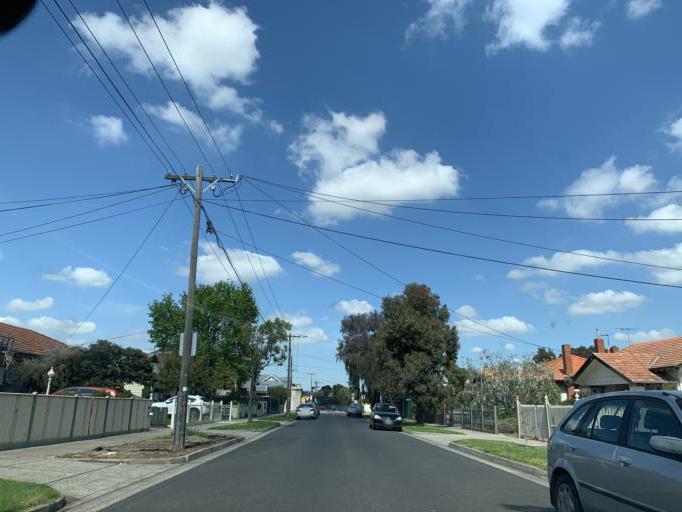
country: AU
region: Victoria
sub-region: Moreland
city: Pascoe Vale South
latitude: -37.7356
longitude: 144.9538
